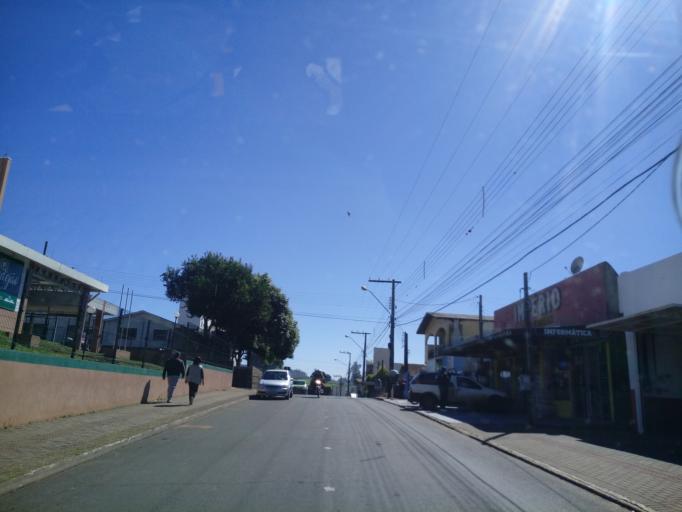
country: BR
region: Santa Catarina
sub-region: Chapeco
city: Chapeco
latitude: -27.0933
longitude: -52.6740
